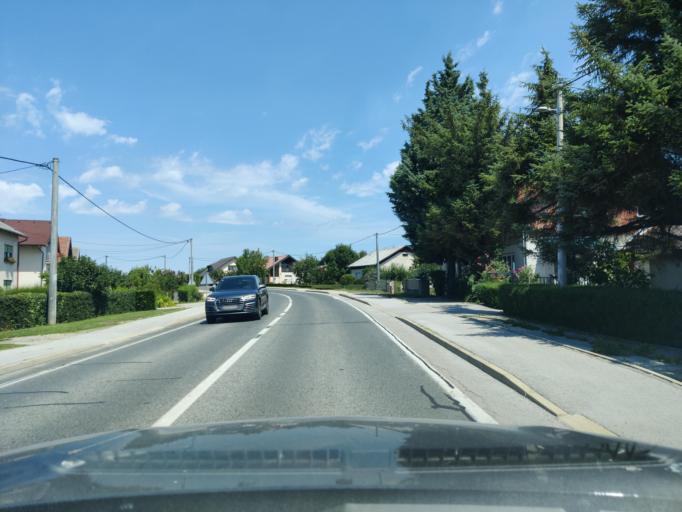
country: HR
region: Medimurska
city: Mackovec
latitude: 46.4301
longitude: 16.4308
